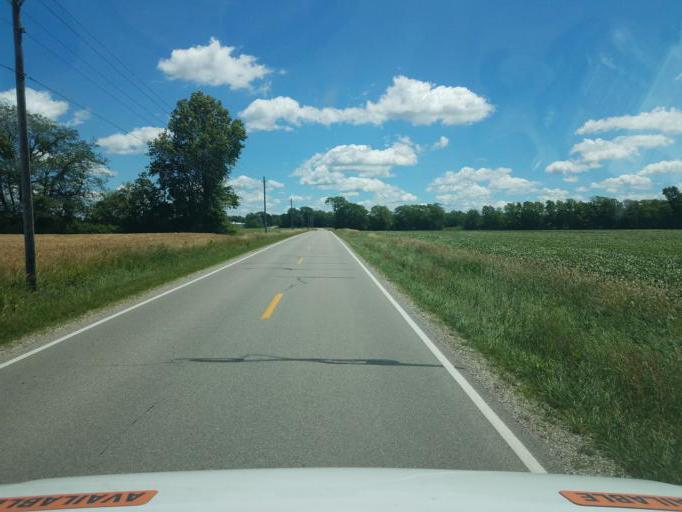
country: US
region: Ohio
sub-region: Crawford County
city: Galion
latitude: 40.7334
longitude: -82.8635
